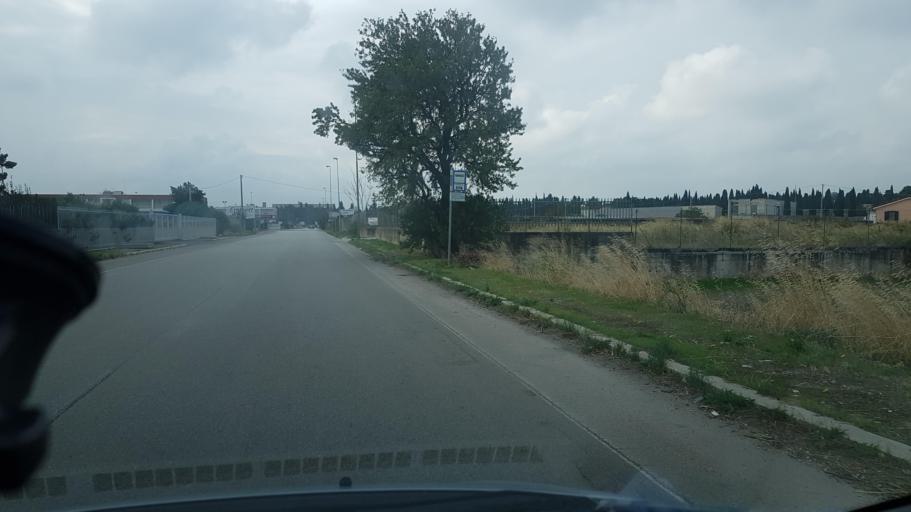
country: IT
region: Apulia
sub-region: Provincia di Foggia
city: Foggia
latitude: 41.4777
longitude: 15.5532
